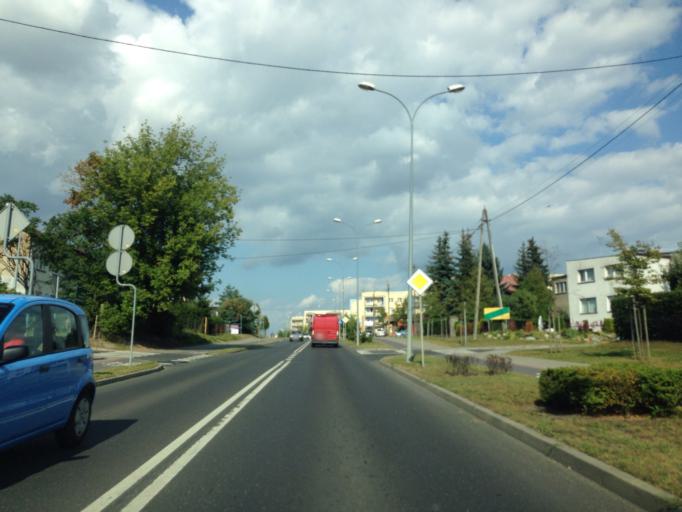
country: PL
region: Warmian-Masurian Voivodeship
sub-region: Powiat ilawski
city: Ilawa
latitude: 53.6023
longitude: 19.5644
